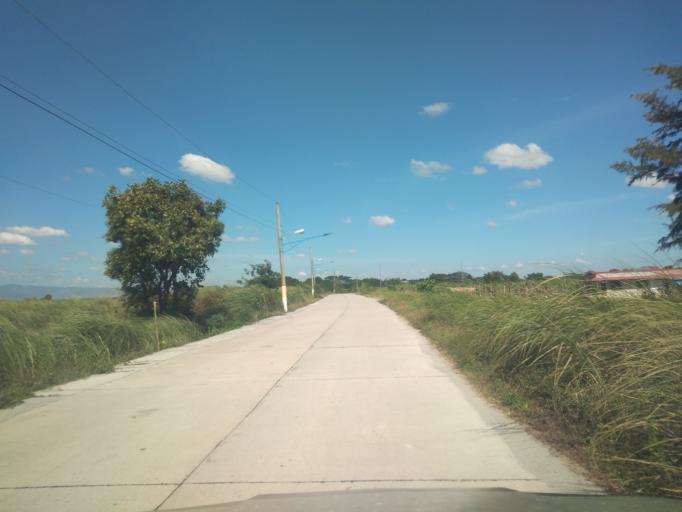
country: PH
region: Central Luzon
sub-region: Province of Pampanga
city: Balas
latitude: 15.0455
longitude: 120.6134
